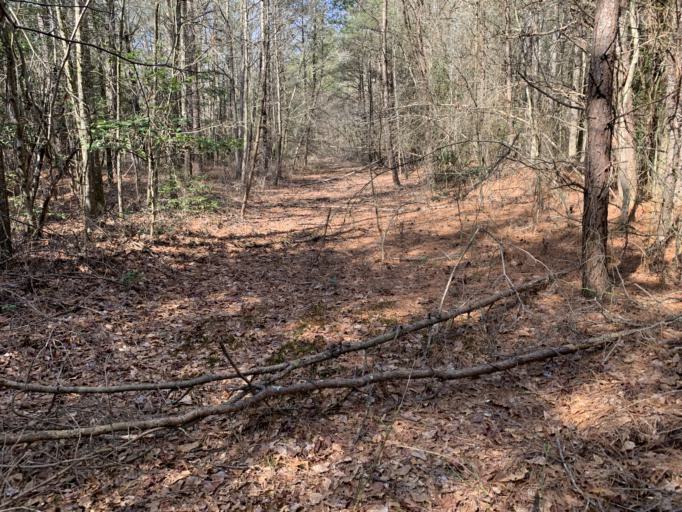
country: US
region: Delaware
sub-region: Sussex County
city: Georgetown
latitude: 38.6834
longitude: -75.4728
